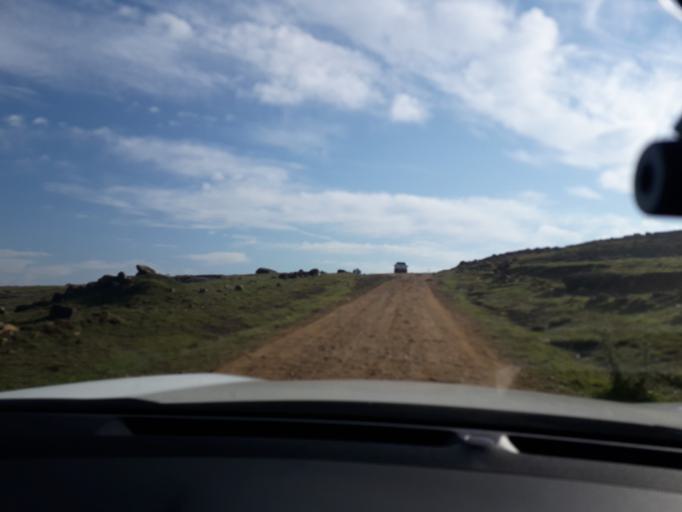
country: ZA
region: Eastern Cape
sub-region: Buffalo City Metropolitan Municipality
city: Bhisho
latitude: -32.9430
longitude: 27.2894
